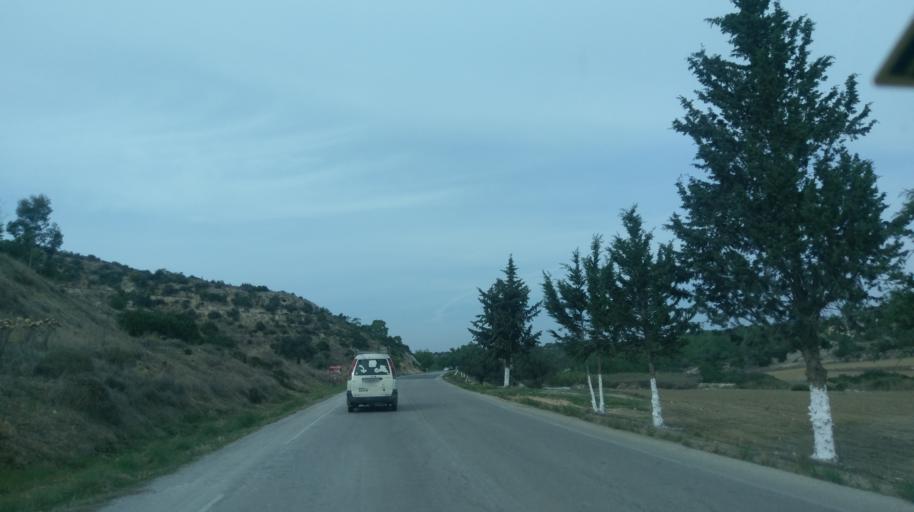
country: CY
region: Ammochostos
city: Leonarisso
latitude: 35.4422
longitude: 34.1363
